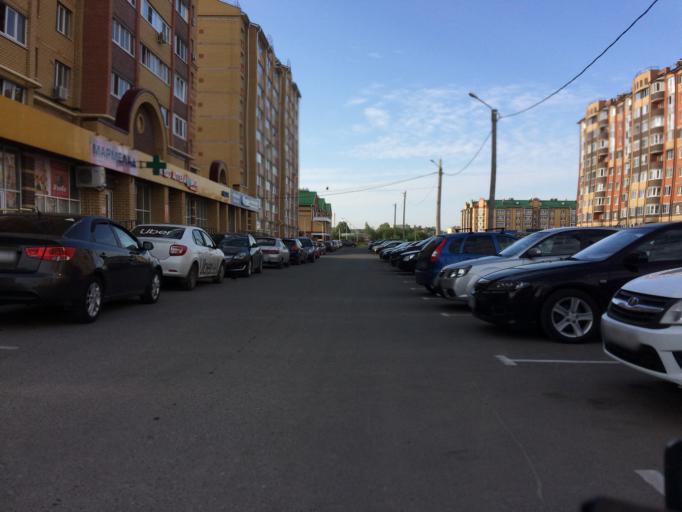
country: RU
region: Mariy-El
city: Medvedevo
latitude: 56.6381
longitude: 47.8125
